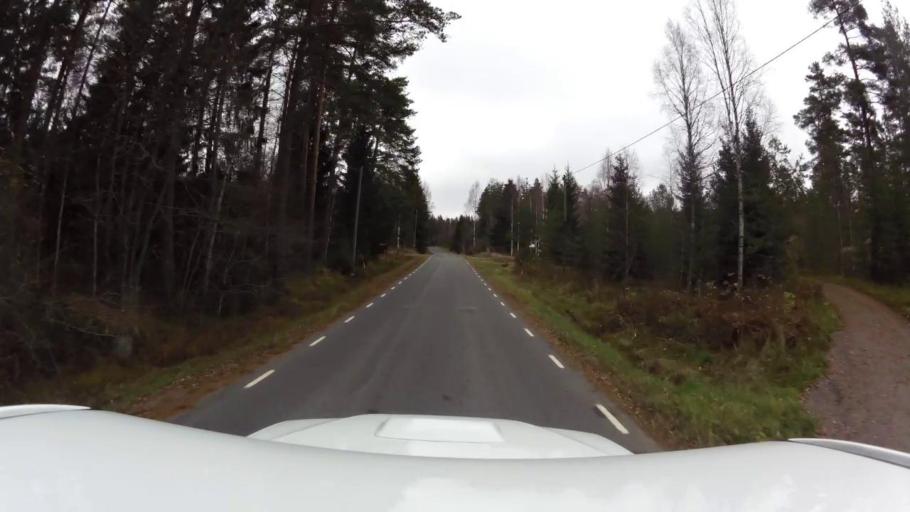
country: SE
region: OEstergoetland
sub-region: Kinda Kommun
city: Kisa
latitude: 58.1344
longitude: 15.4524
